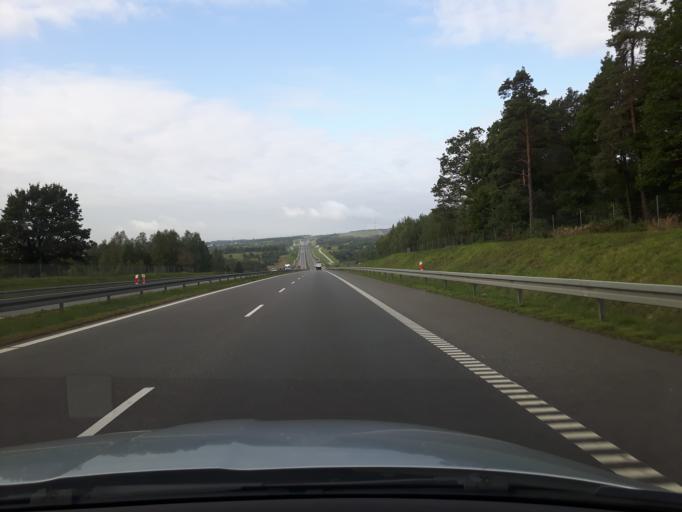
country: PL
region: Swietokrzyskie
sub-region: Powiat skarzyski
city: Laczna
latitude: 51.0065
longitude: 20.8019
